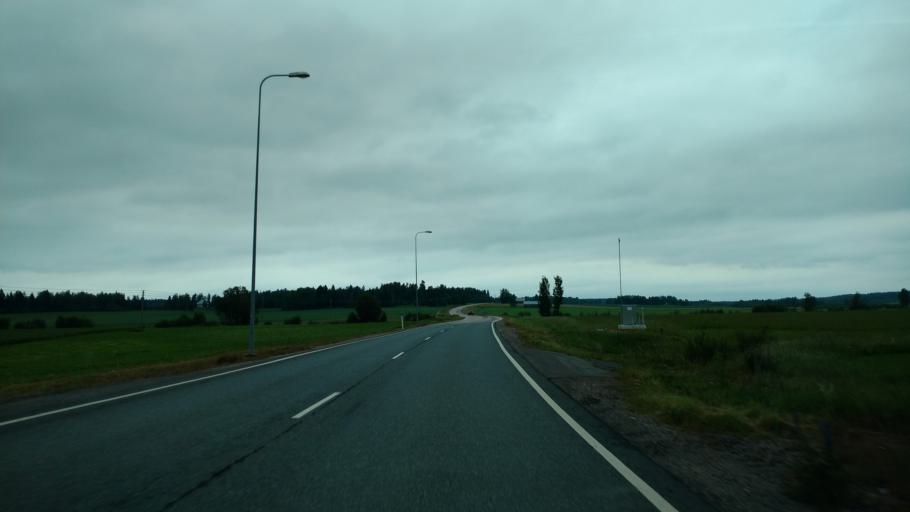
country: FI
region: Varsinais-Suomi
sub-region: Salo
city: Kiikala
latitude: 60.3942
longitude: 23.5851
